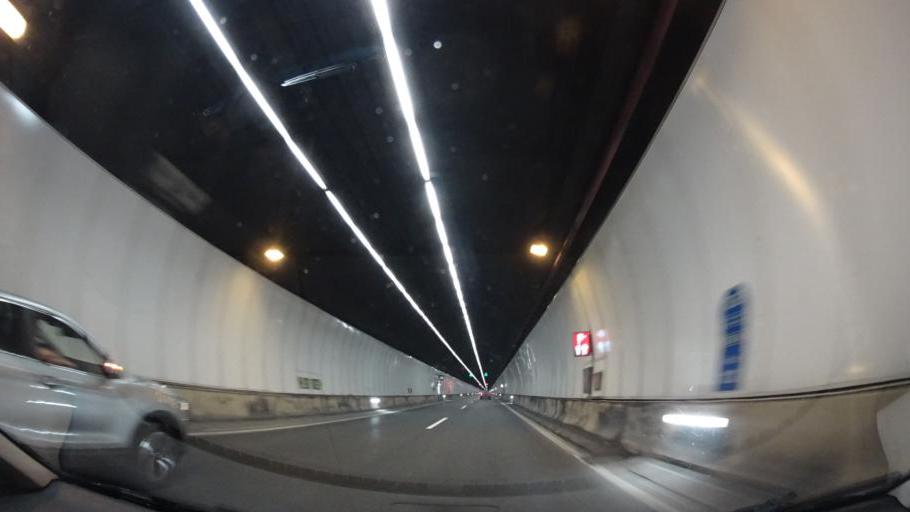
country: ES
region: Basque Country
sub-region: Bizkaia
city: Basauri
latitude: 43.2322
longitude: -2.8954
